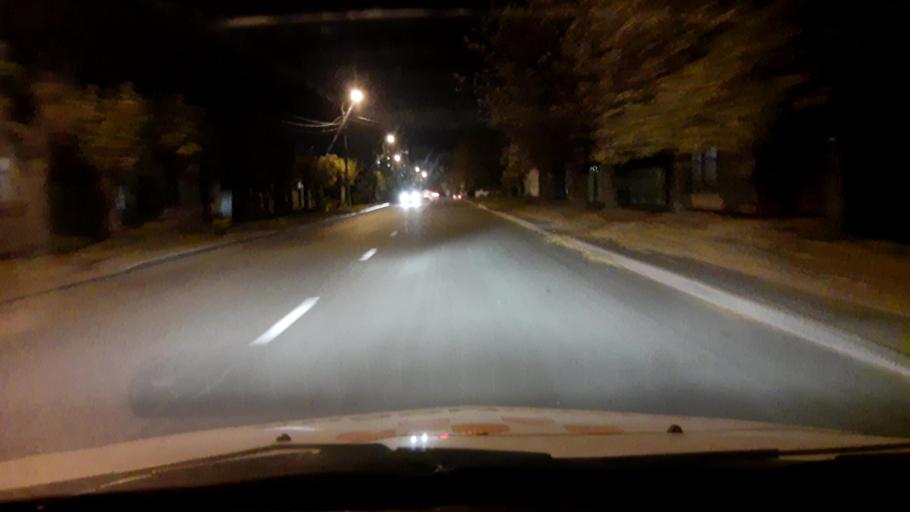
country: RU
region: Bashkortostan
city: Ufa
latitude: 54.7209
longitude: 55.9696
